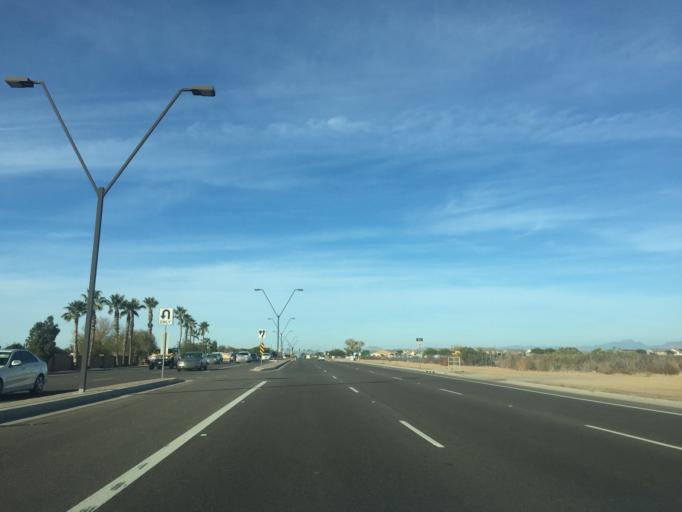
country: US
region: Arizona
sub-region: Maricopa County
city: Queen Creek
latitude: 33.2228
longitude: -111.6344
